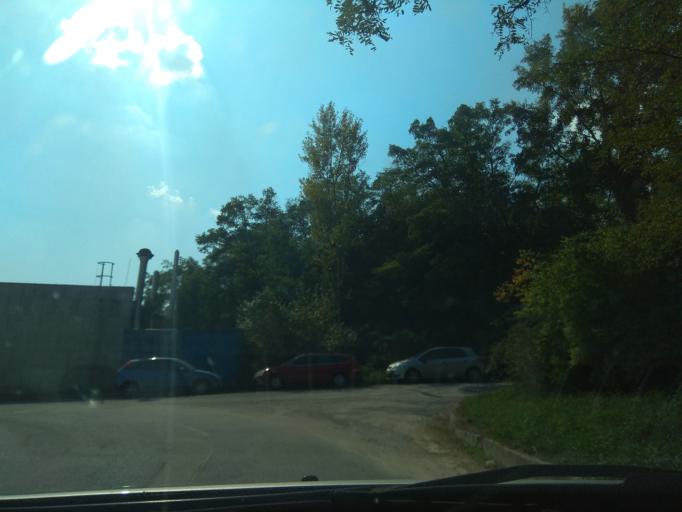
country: HU
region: Borsod-Abauj-Zemplen
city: Miskolc
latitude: 48.0817
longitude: 20.7625
